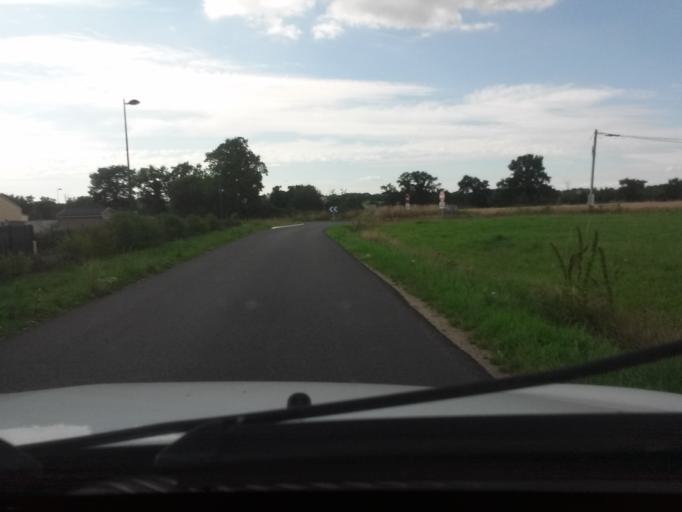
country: FR
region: Pays de la Loire
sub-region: Departement de la Vendee
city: La Bruffiere
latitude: 47.0126
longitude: -1.1851
